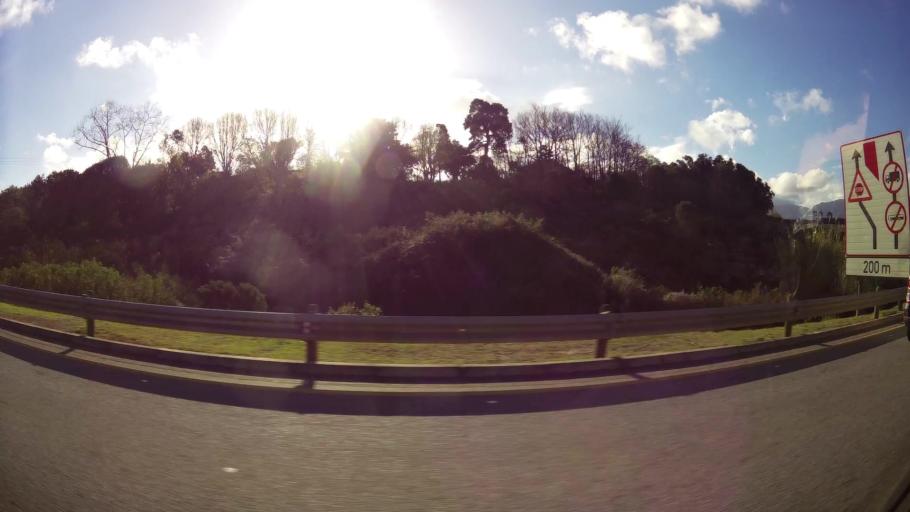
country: ZA
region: Western Cape
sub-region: Eden District Municipality
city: George
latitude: -33.9925
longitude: 22.5341
